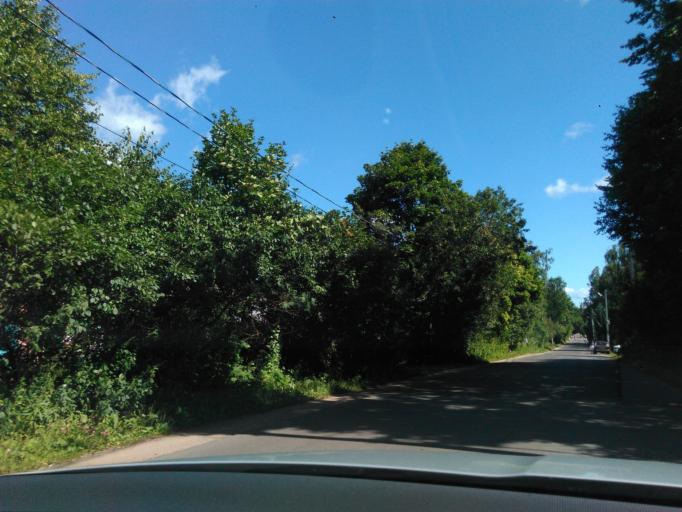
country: RU
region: Moskovskaya
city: Klin
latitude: 56.2342
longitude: 36.8231
